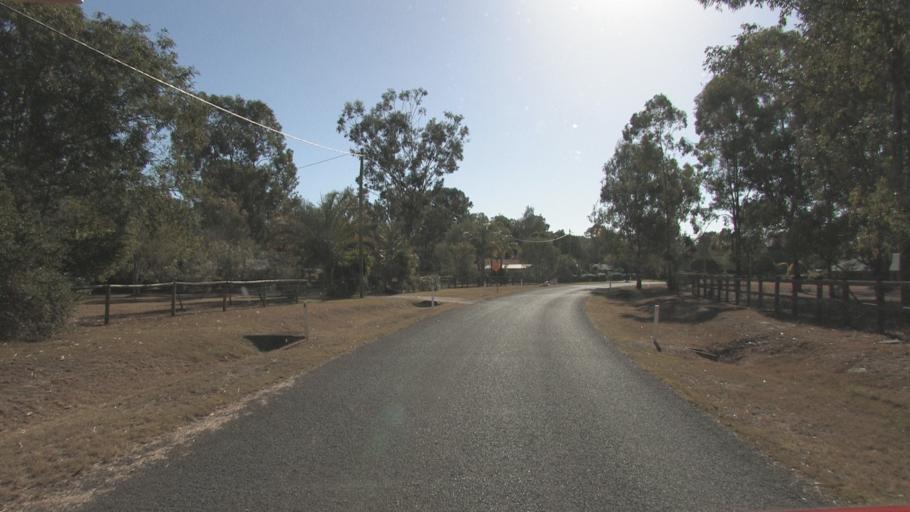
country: AU
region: Queensland
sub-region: Logan
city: North Maclean
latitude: -27.8277
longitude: 152.9904
